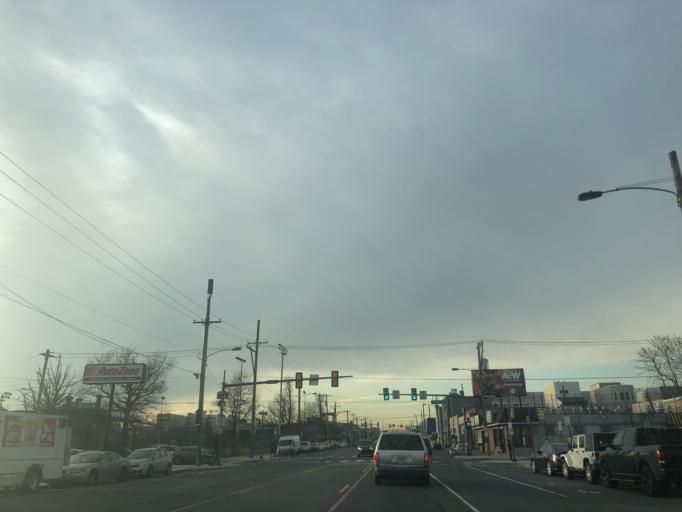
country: US
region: Pennsylvania
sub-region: Philadelphia County
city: Philadelphia
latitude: 39.9386
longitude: -75.1725
